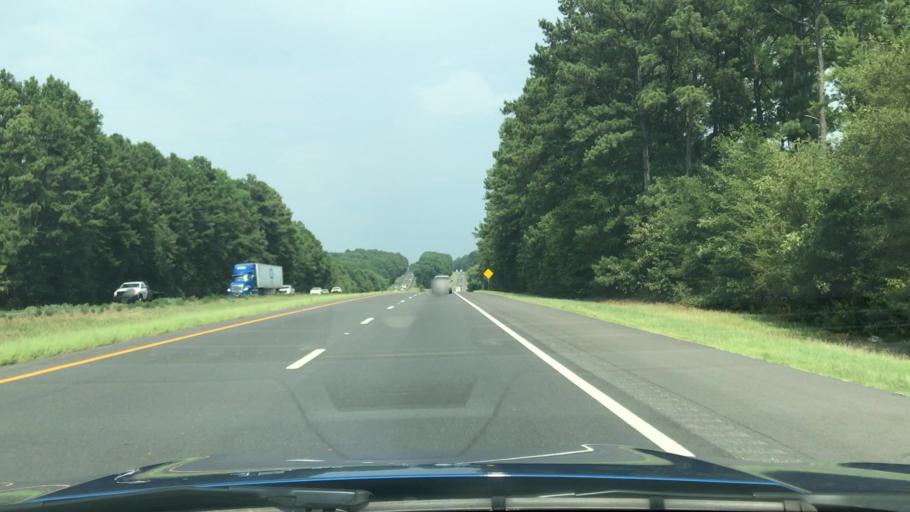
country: US
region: Texas
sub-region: Harrison County
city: Hallsville
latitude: 32.4684
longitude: -94.6096
